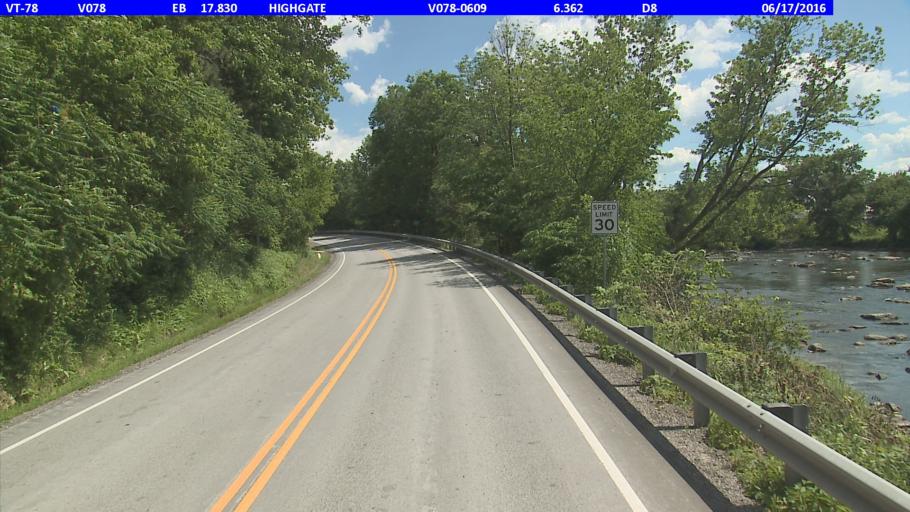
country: US
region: Vermont
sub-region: Franklin County
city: Swanton
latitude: 44.9316
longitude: -72.9893
